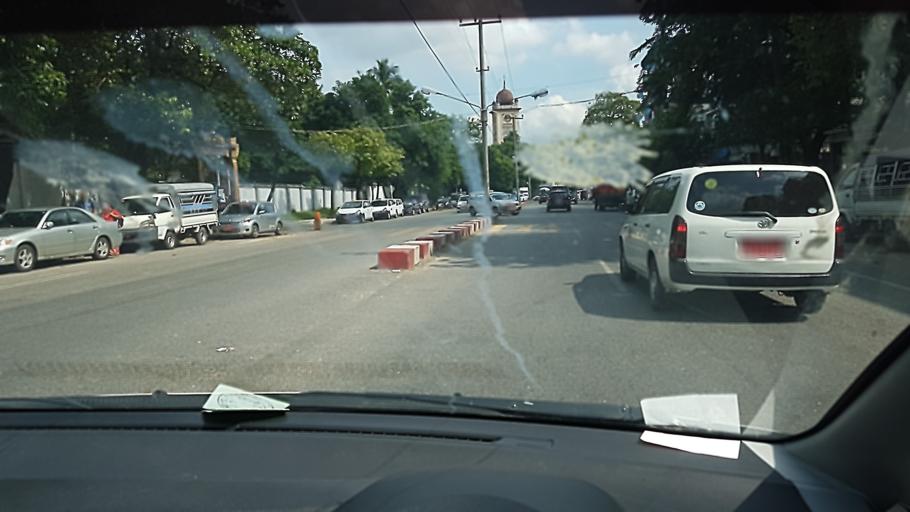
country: MM
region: Yangon
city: Yangon
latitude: 16.8004
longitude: 96.1733
